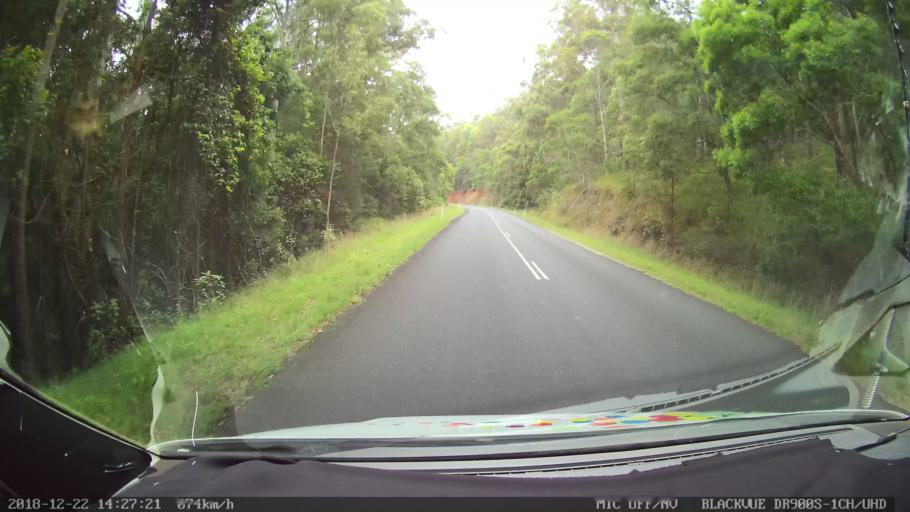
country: AU
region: New South Wales
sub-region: Bellingen
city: Dorrigo
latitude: -30.0646
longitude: 152.6345
